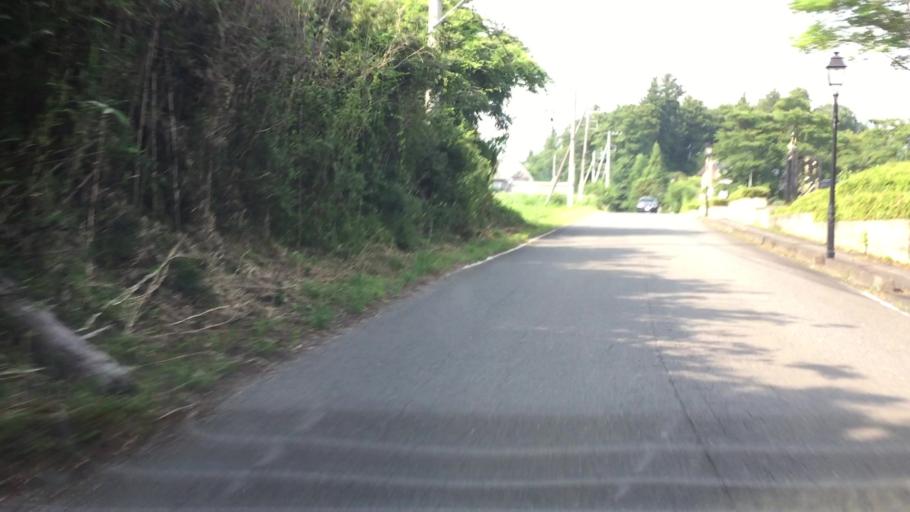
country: JP
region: Tochigi
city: Kuroiso
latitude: 37.0440
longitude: 140.0273
